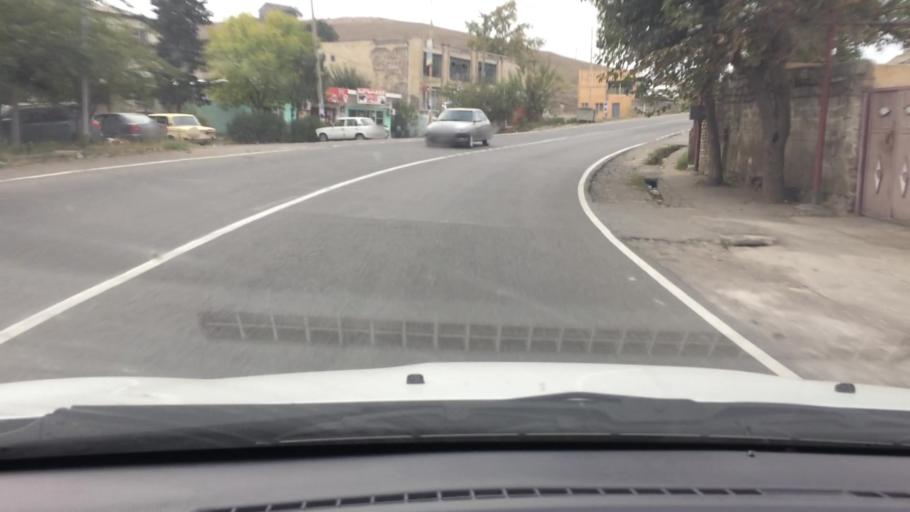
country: GE
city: Naghvarevi
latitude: 41.3659
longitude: 44.8402
